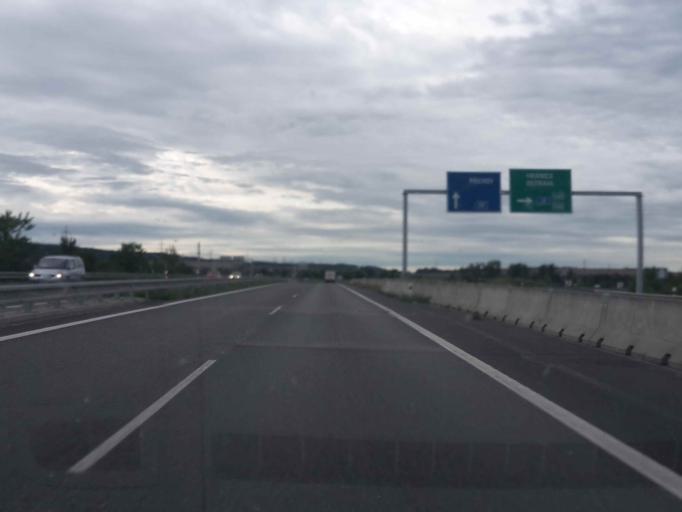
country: CZ
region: Olomoucky
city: Velky Tynec
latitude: 49.5594
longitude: 17.3153
